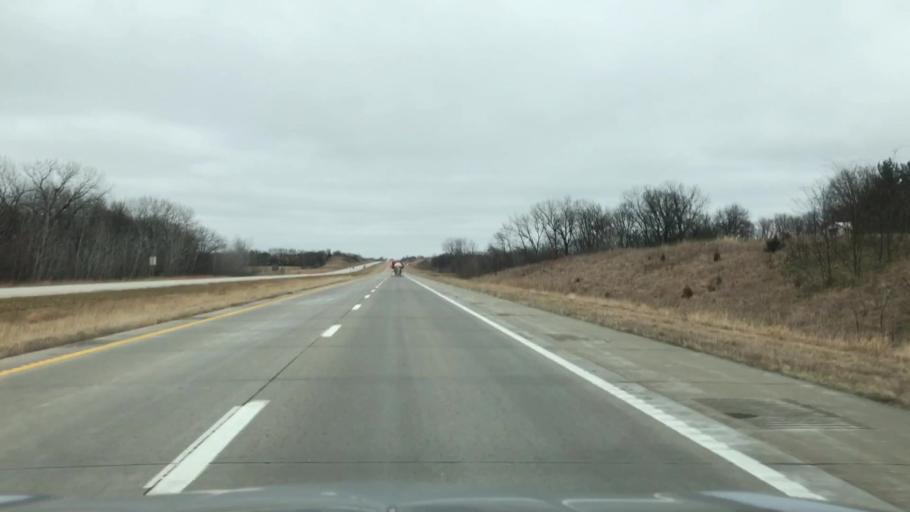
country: US
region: Missouri
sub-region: Caldwell County
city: Hamilton
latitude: 39.7343
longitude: -93.9678
